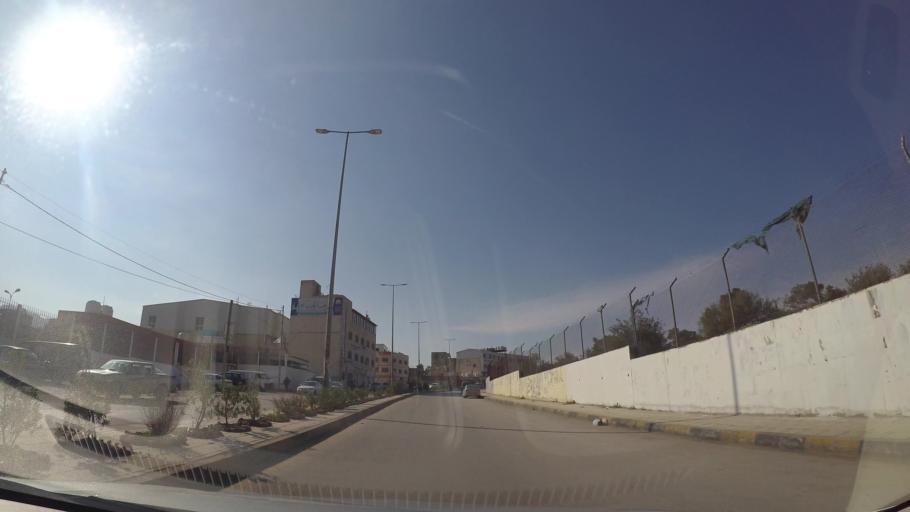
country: JO
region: Amman
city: Al Jubayhah
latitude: 32.0795
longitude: 35.8453
